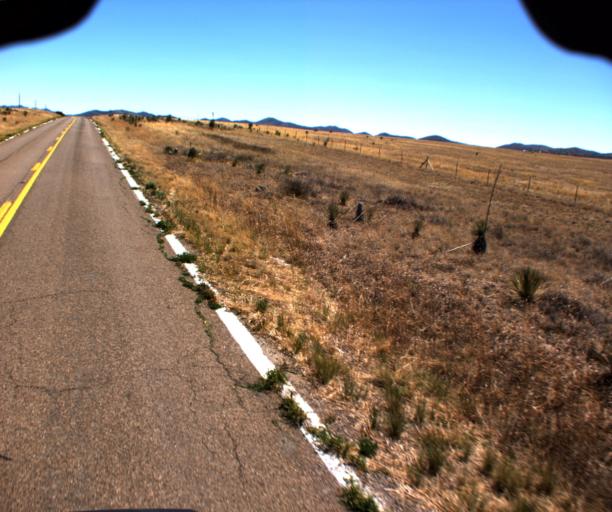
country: US
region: Arizona
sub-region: Cochise County
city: Huachuca City
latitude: 31.6313
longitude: -110.5954
